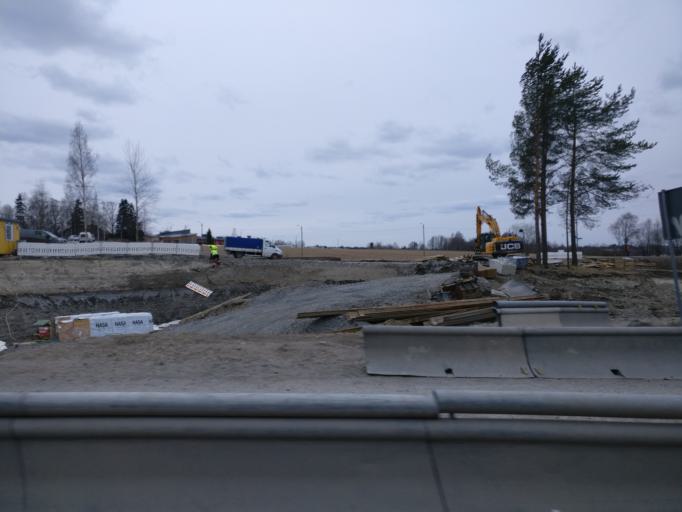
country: FI
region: Pirkanmaa
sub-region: Tampere
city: Tampere
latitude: 61.4810
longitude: 23.8295
